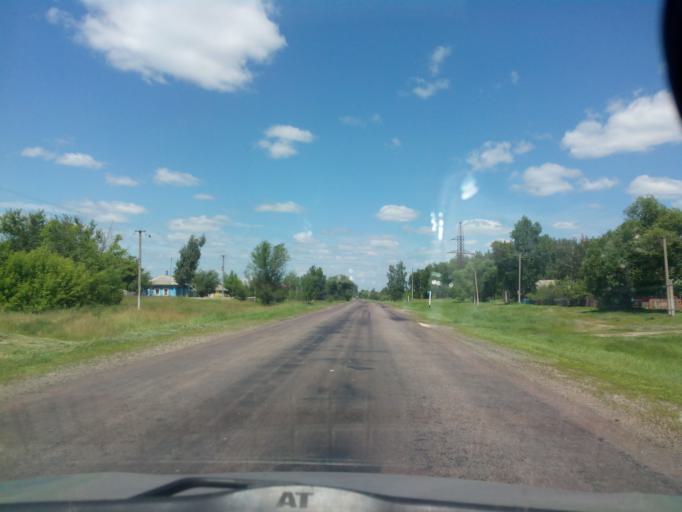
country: RU
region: Tambov
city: Zherdevka
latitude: 51.7351
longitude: 41.5161
